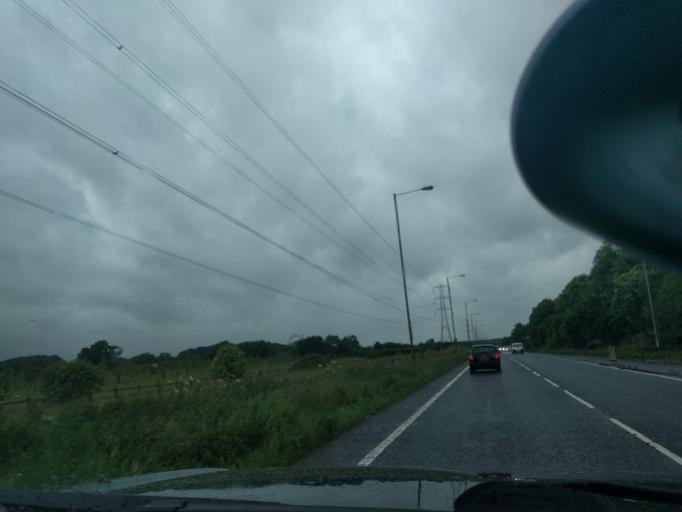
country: GB
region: England
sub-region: Wiltshire
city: Chippenham
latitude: 51.4548
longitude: -2.1518
